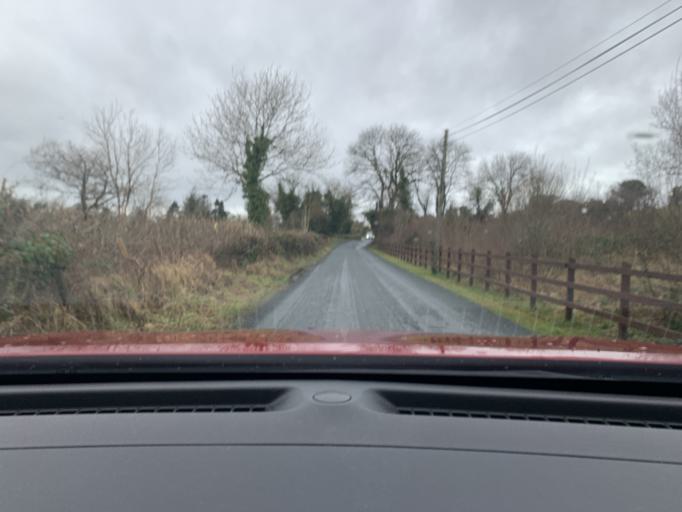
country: IE
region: Connaught
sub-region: Sligo
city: Collooney
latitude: 54.2024
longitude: -8.4296
